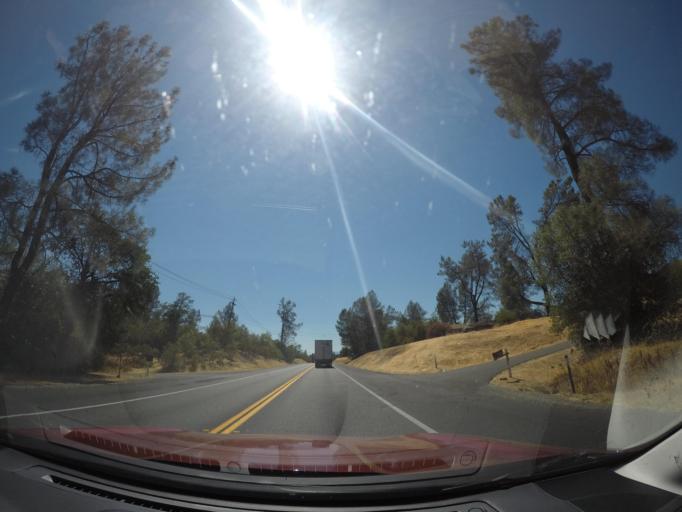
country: US
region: California
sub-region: Shasta County
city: Bella Vista
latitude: 40.6293
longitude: -122.2795
